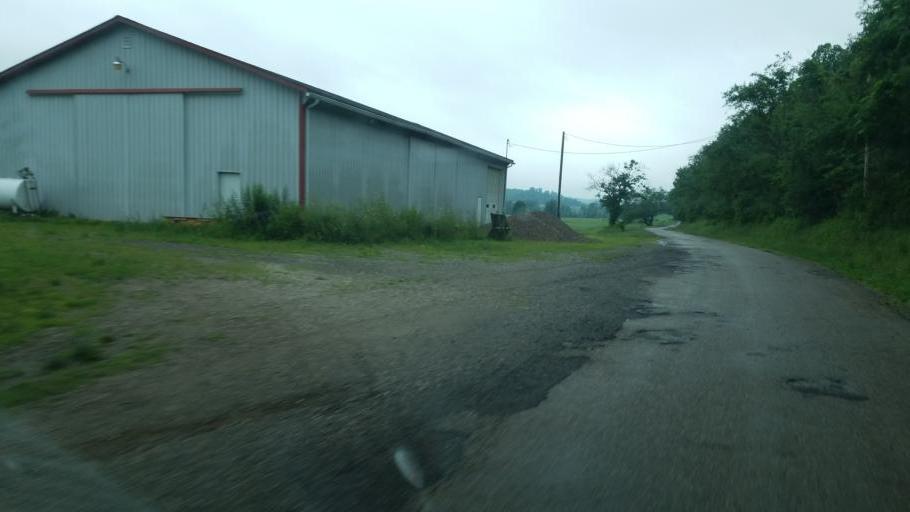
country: US
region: Ohio
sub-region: Tuscarawas County
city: Dennison
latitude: 40.3789
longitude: -81.2470
